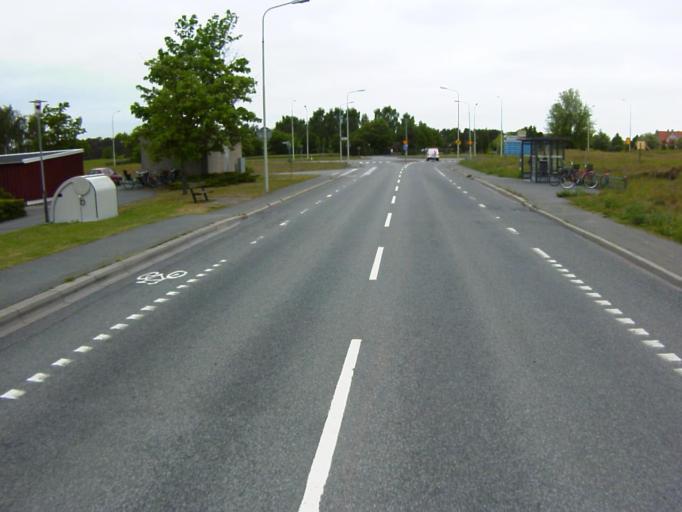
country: SE
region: Skane
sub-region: Kristianstads Kommun
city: Ahus
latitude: 55.9202
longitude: 14.2854
